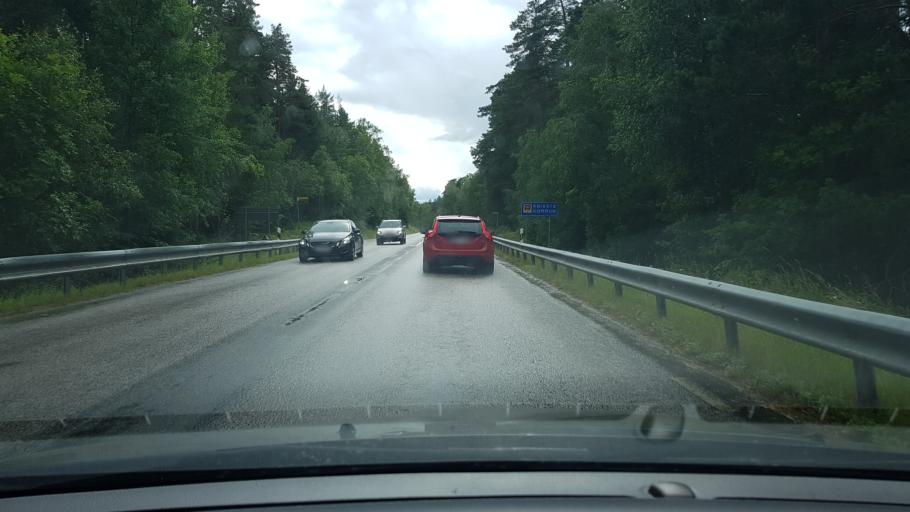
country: SE
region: Uppsala
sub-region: Uppsala Kommun
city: Saevja
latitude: 59.7931
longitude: 17.6754
